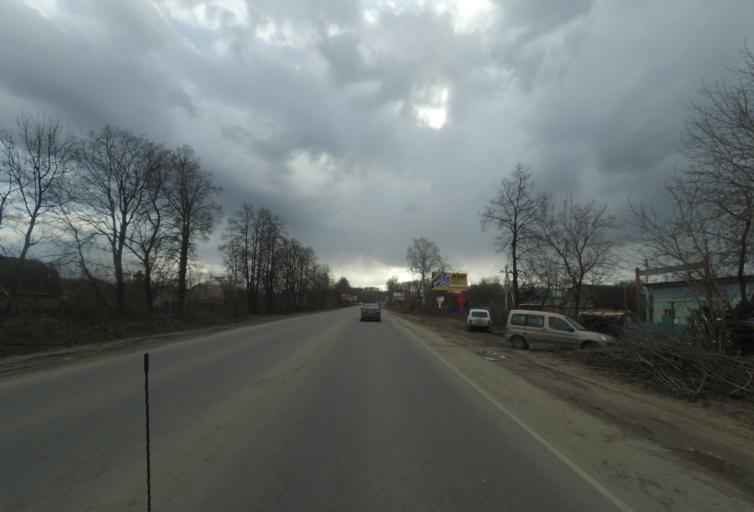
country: RU
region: Nizjnij Novgorod
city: Afonino
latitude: 56.2235
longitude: 44.0881
